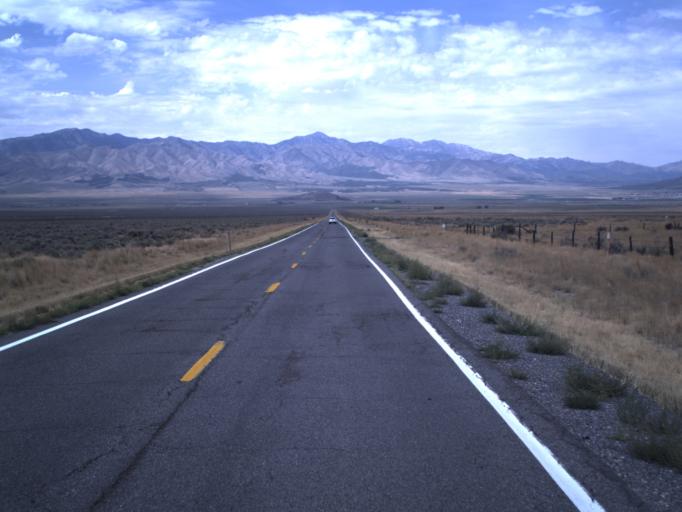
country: US
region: Utah
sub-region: Tooele County
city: Tooele
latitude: 40.3634
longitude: -112.3362
